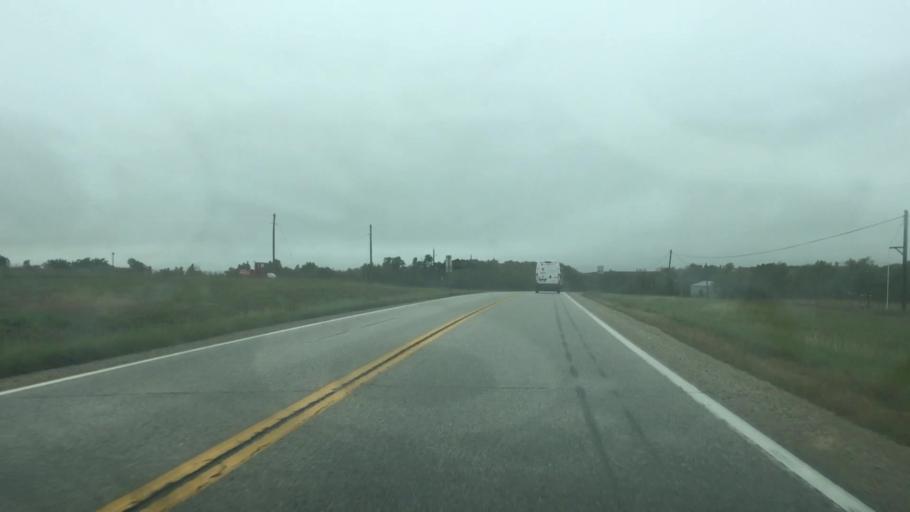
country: US
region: Kansas
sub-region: Anderson County
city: Garnett
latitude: 38.1952
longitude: -95.2516
